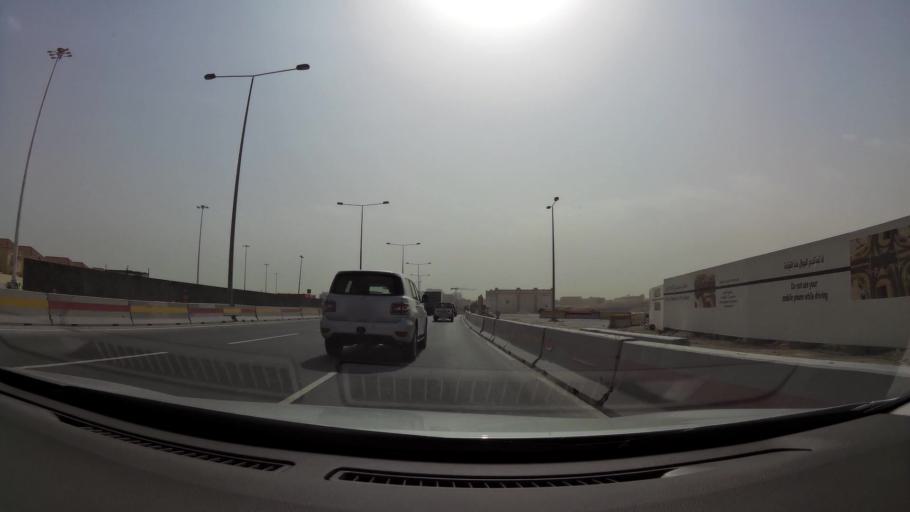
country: QA
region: Baladiyat ad Dawhah
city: Doha
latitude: 25.2934
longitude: 51.4867
